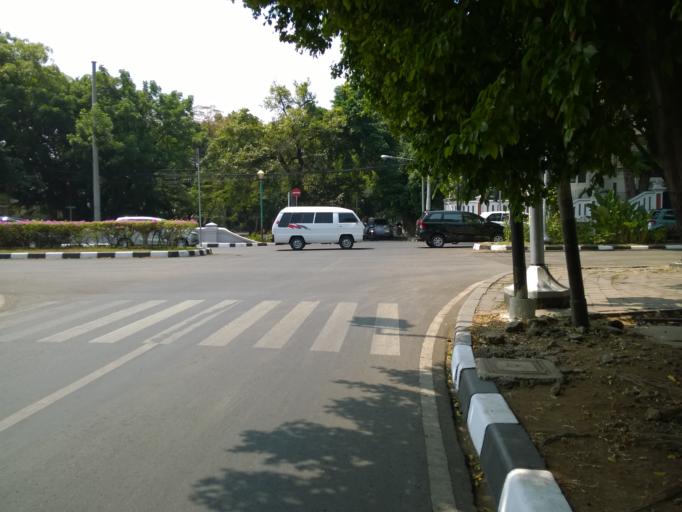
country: ID
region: Jakarta Raya
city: Jakarta
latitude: -6.1960
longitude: 106.8328
